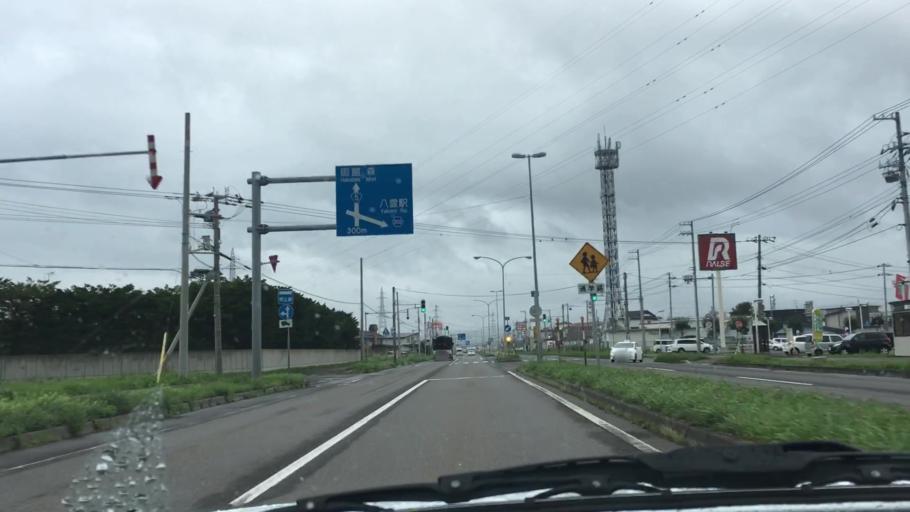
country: JP
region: Hokkaido
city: Nanae
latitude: 42.2592
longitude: 140.2773
